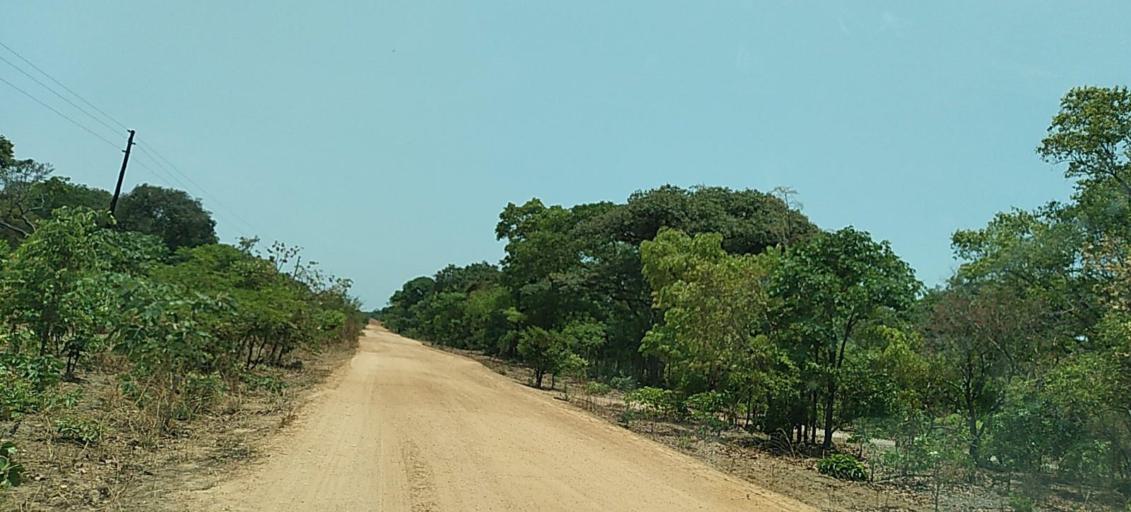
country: ZM
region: Copperbelt
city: Mpongwe
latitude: -13.8004
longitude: 27.8598
